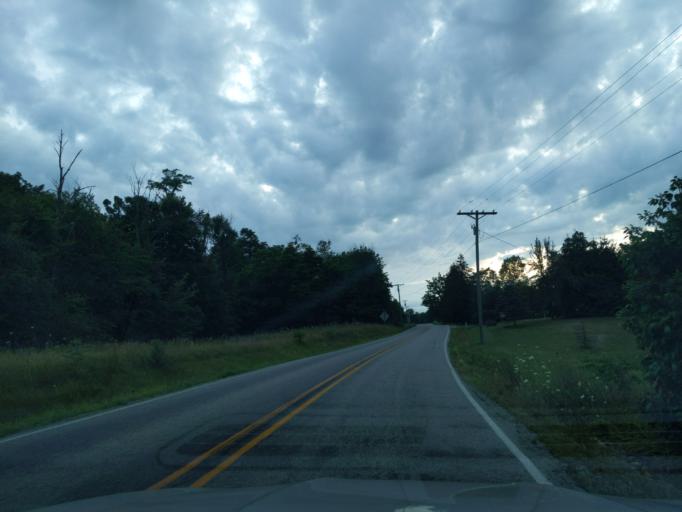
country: US
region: Indiana
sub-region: Ripley County
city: Osgood
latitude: 39.1946
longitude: -85.2616
